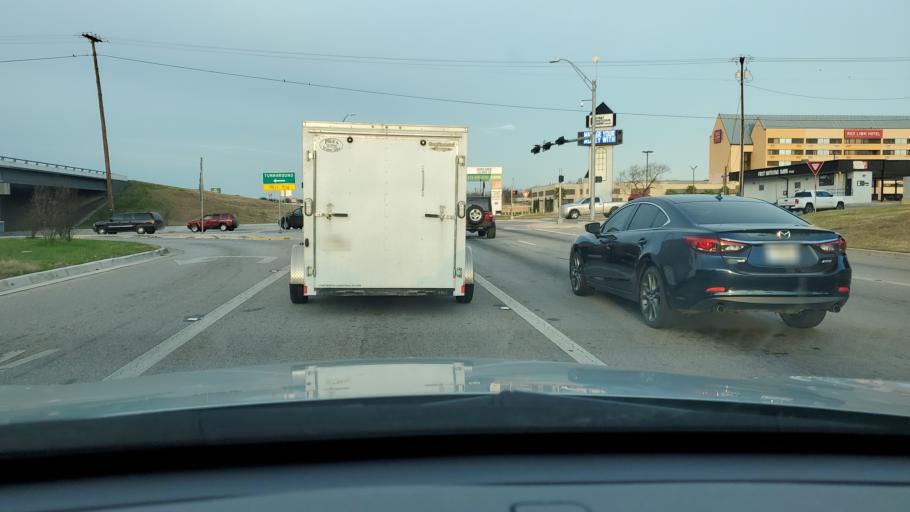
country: US
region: Texas
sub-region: Bell County
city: Killeen
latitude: 31.0950
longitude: -97.7316
